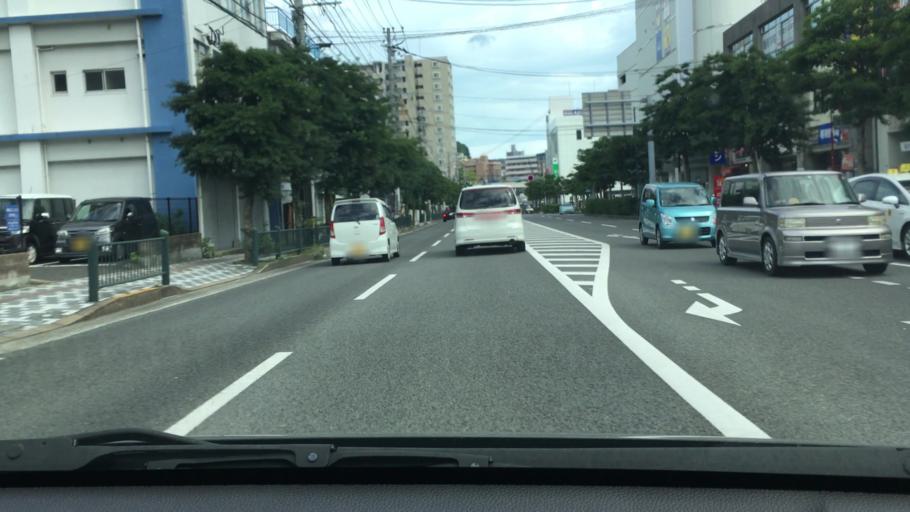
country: JP
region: Nagasaki
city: Togitsu
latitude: 32.8047
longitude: 129.8508
